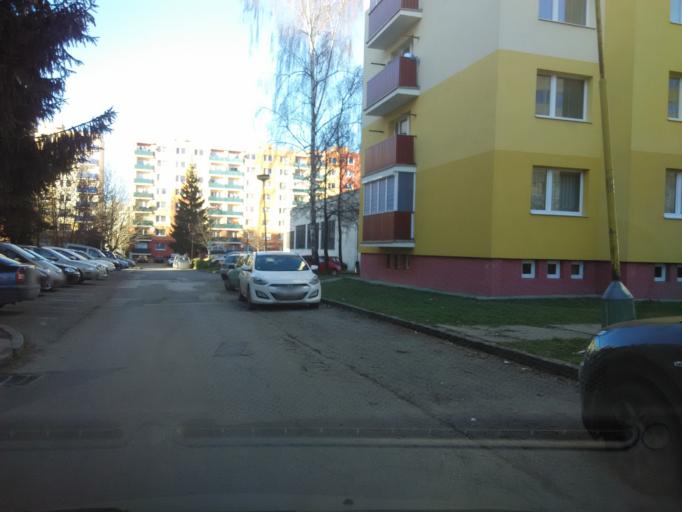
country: SK
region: Zilinsky
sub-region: Okres Zilina
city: Zilina
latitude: 49.2059
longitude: 18.7675
